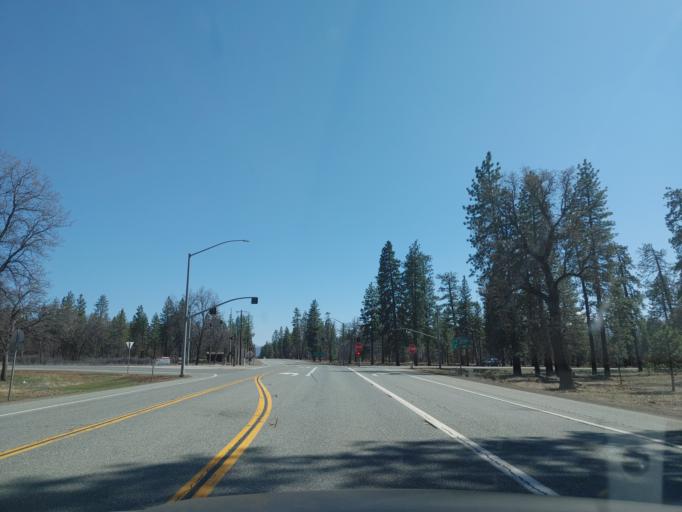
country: US
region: California
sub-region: Shasta County
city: Burney
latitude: 40.9389
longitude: -121.6070
